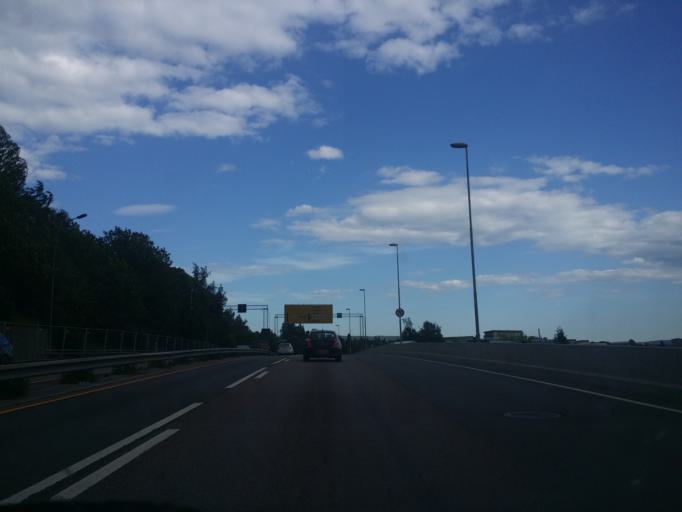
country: NO
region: Oslo
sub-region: Oslo
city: Oslo
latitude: 59.9525
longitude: 10.7711
